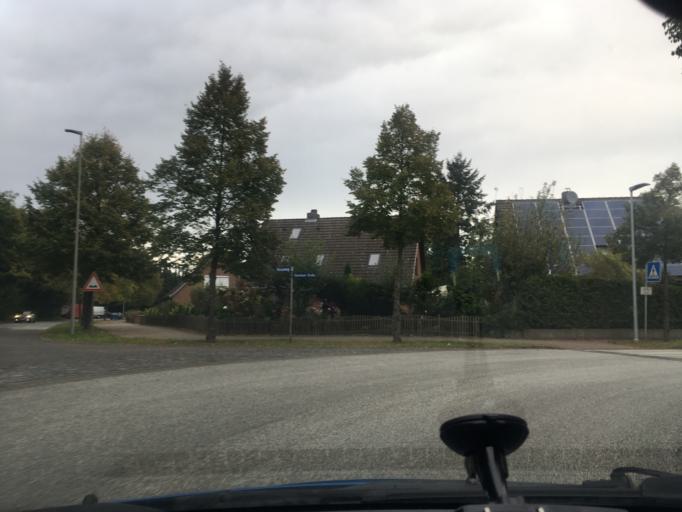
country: DE
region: Schleswig-Holstein
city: Escheburg
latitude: 53.4350
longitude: 10.3386
